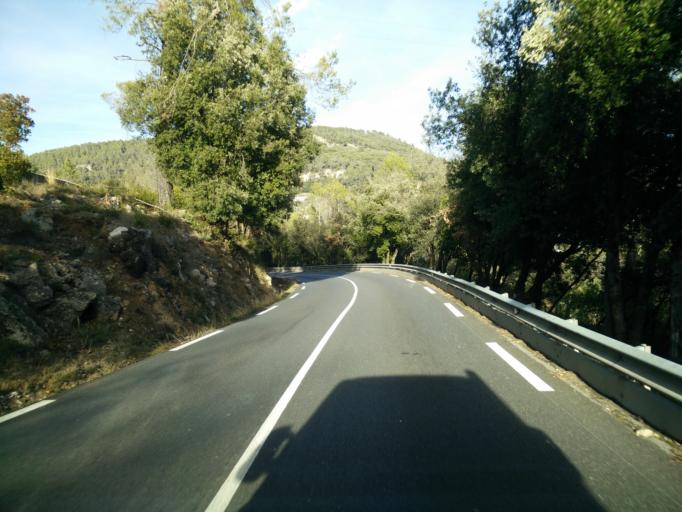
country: FR
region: Provence-Alpes-Cote d'Azur
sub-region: Departement des Alpes-Maritimes
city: Le Tignet
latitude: 43.6199
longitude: 6.8239
